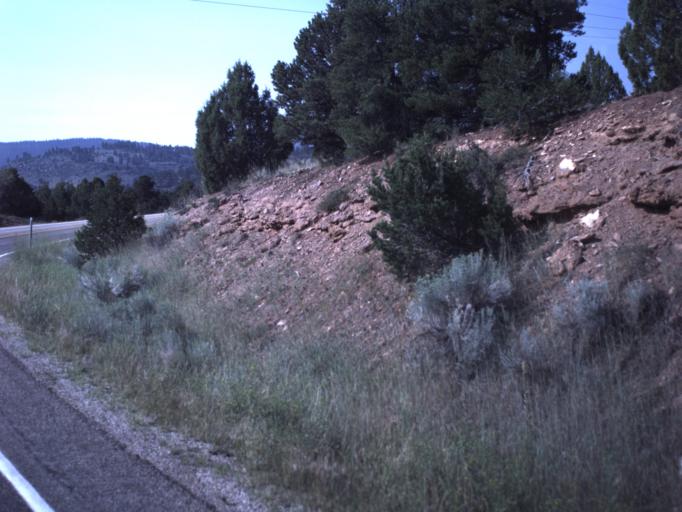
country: US
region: Utah
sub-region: Daggett County
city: Manila
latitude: 40.9061
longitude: -109.4378
